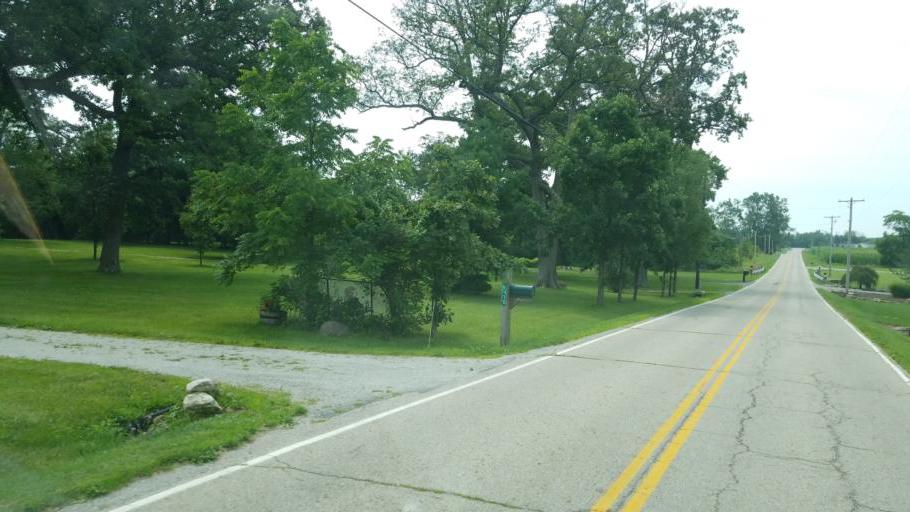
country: US
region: Ohio
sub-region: Madison County
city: Choctaw Lake
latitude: 40.0176
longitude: -83.3904
